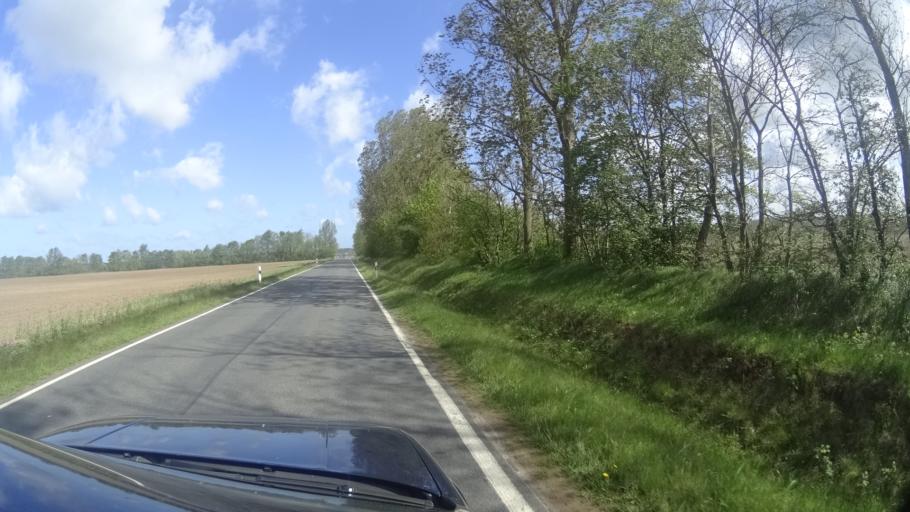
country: DE
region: Mecklenburg-Vorpommern
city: Born
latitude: 54.3264
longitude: 12.5857
